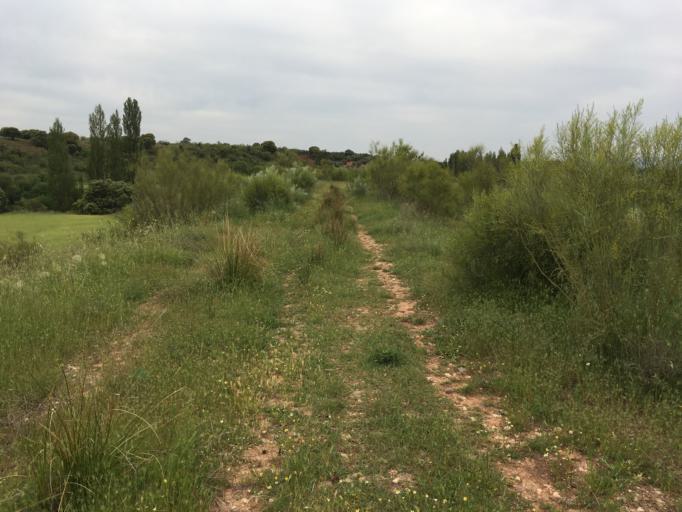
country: ES
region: Castille-La Mancha
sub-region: Provincia de Albacete
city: Alcaraz
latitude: 38.6967
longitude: -2.4818
